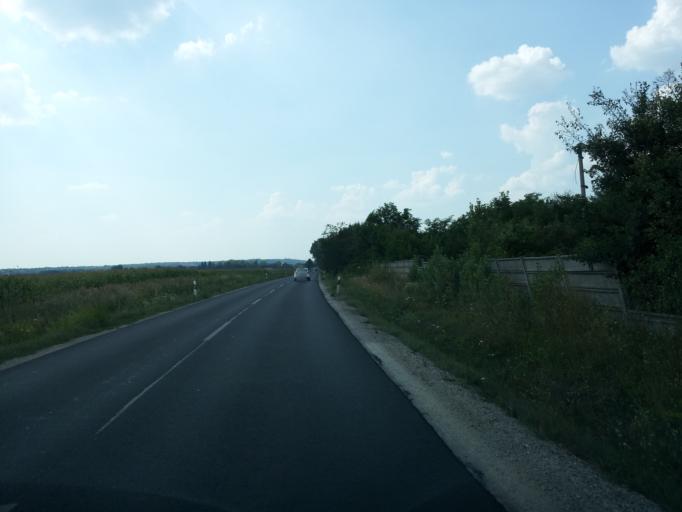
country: HU
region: Pest
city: Szigethalom
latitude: 47.3348
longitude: 18.9865
